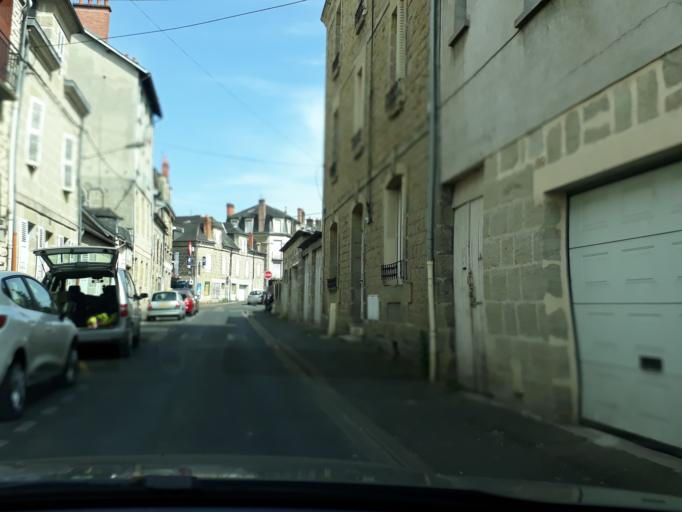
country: FR
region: Limousin
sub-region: Departement de la Correze
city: Brive-la-Gaillarde
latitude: 45.1567
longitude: 1.5255
